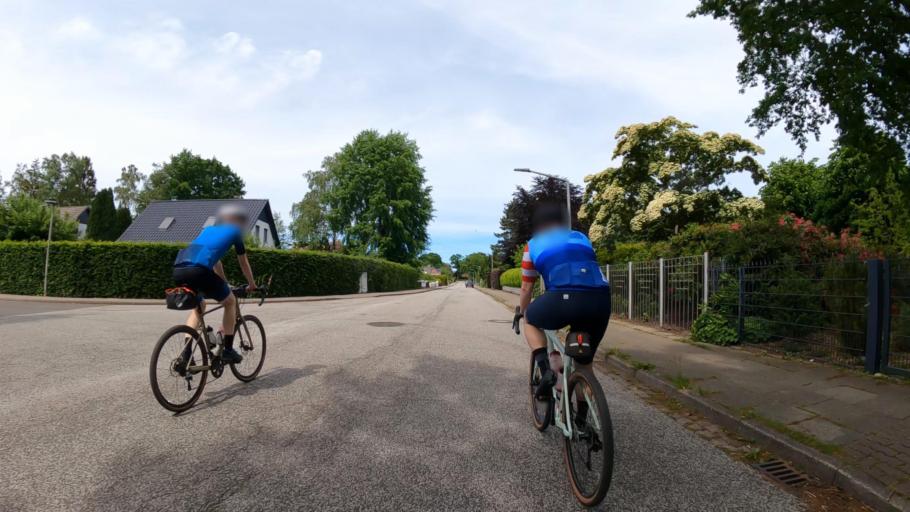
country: DE
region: Schleswig-Holstein
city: Henstedt-Ulzburg
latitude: 53.7553
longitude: 10.0055
